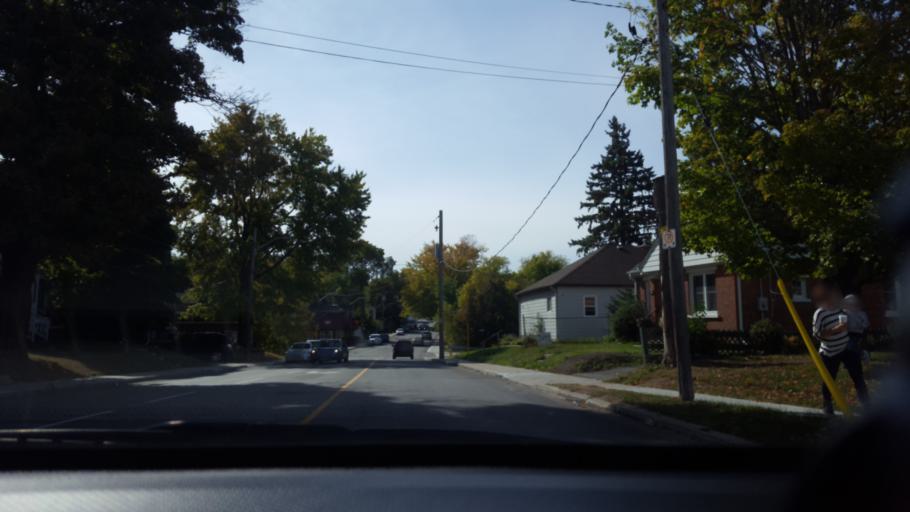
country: CA
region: Ontario
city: Newmarket
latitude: 44.0577
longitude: -79.4535
